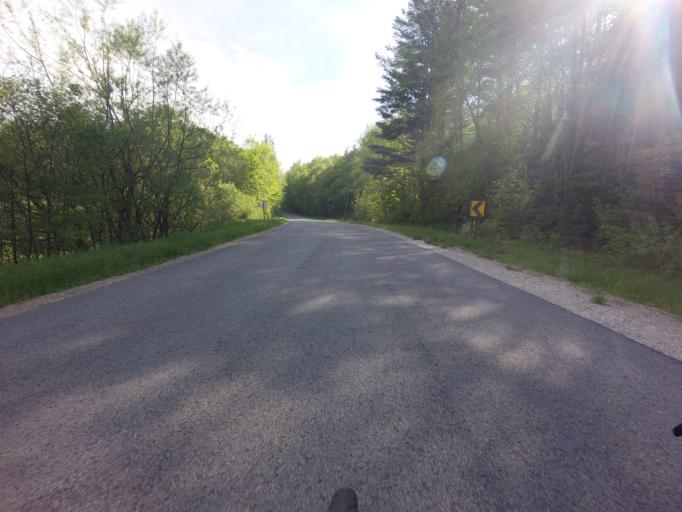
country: US
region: New York
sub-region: St. Lawrence County
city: Gouverneur
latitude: 44.2091
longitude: -75.2492
